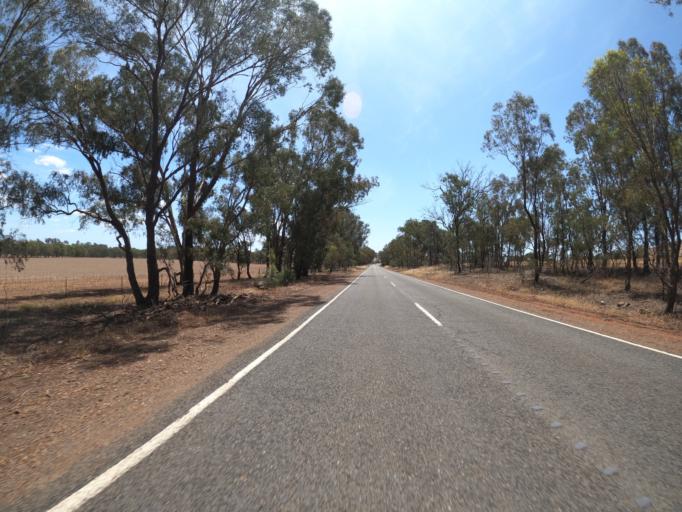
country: AU
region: Victoria
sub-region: Benalla
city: Benalla
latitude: -36.3460
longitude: 145.9606
